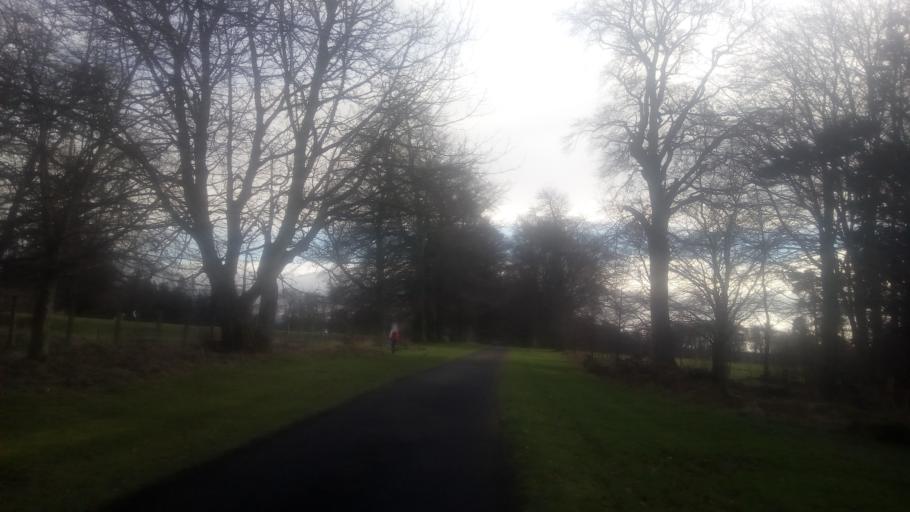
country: GB
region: Scotland
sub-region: The Scottish Borders
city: Duns
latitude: 55.7798
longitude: -2.3539
